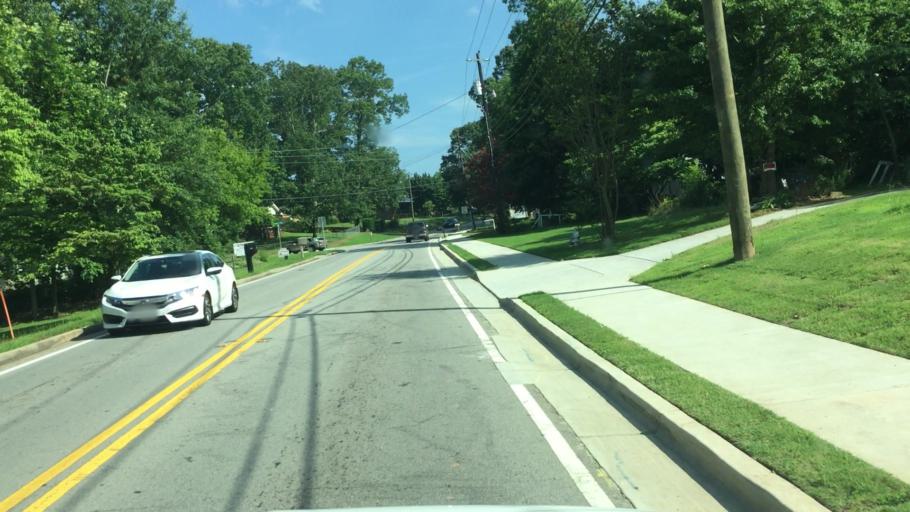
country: US
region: Georgia
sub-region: Gwinnett County
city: Dacula
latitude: 33.9859
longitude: -83.8928
